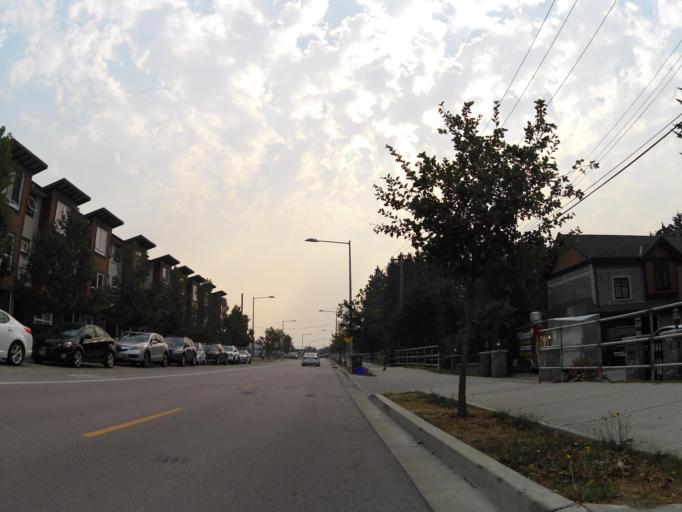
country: CA
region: British Columbia
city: Richmond
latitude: 49.1976
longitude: -123.1067
